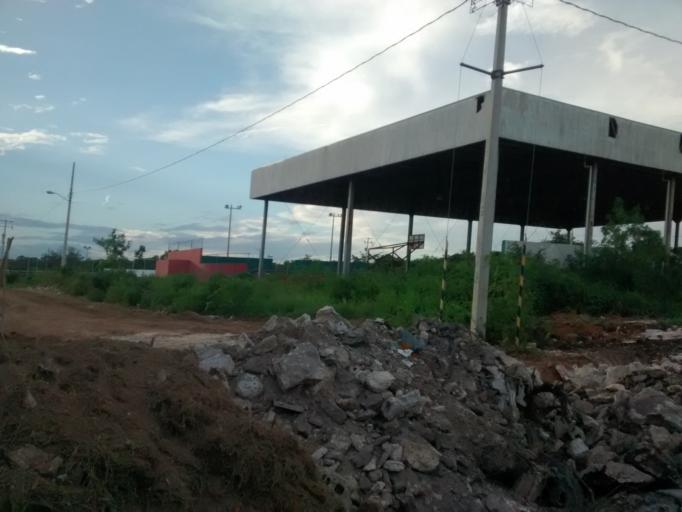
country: MX
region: Yucatan
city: Valladolid
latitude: 20.6860
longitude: -88.1795
